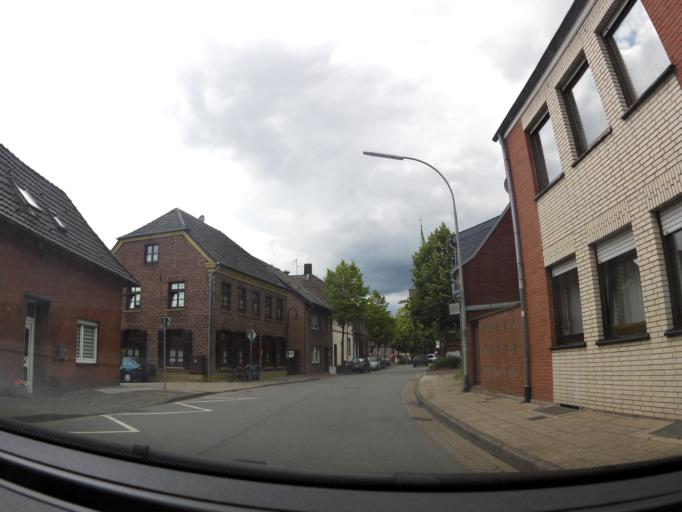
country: DE
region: North Rhine-Westphalia
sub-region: Regierungsbezirk Dusseldorf
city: Sonsbeck
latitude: 51.5701
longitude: 6.3646
